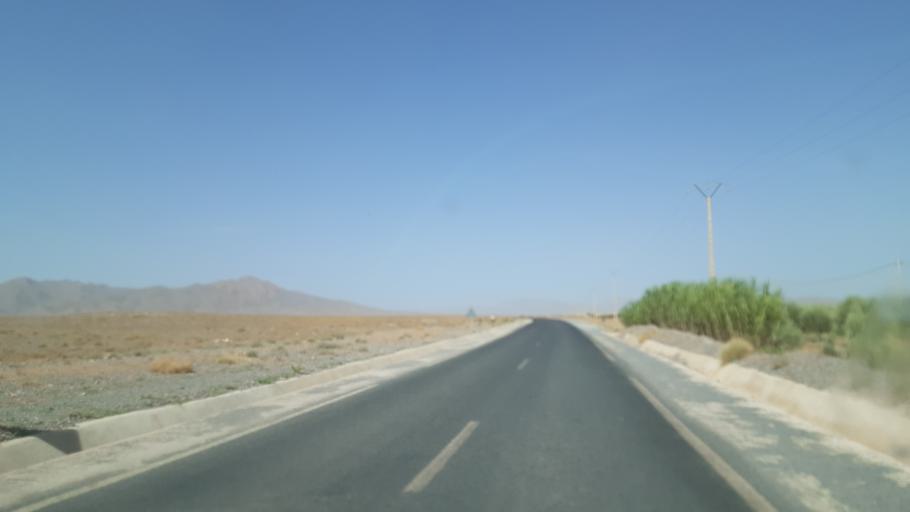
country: MA
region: Meknes-Tafilalet
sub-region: Errachidia
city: Amouguer
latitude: 32.2363
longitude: -4.6261
